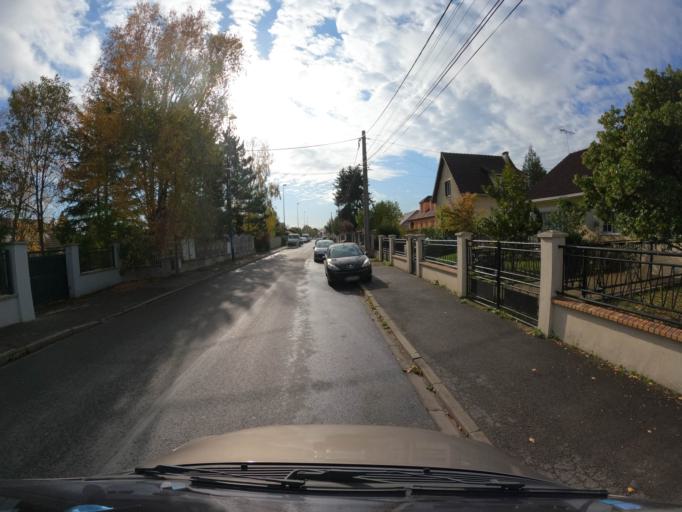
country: FR
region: Ile-de-France
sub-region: Departement de Seine-et-Marne
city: Chelles
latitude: 48.8921
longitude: 2.6033
